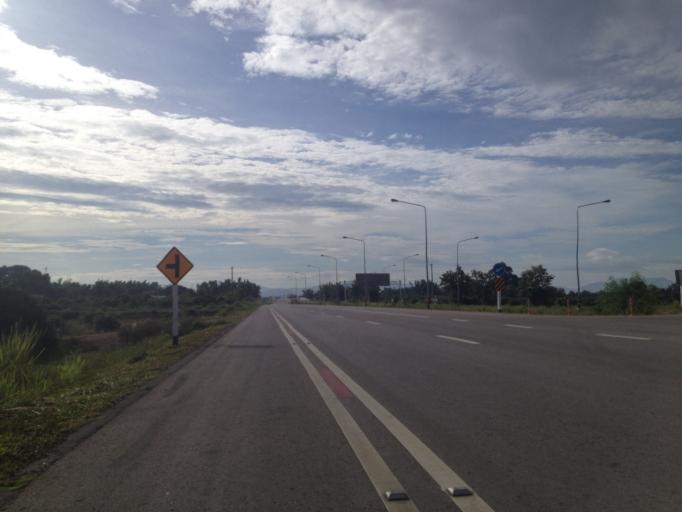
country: TH
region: Lamphun
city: Pa Sang
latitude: 18.5422
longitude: 98.8533
